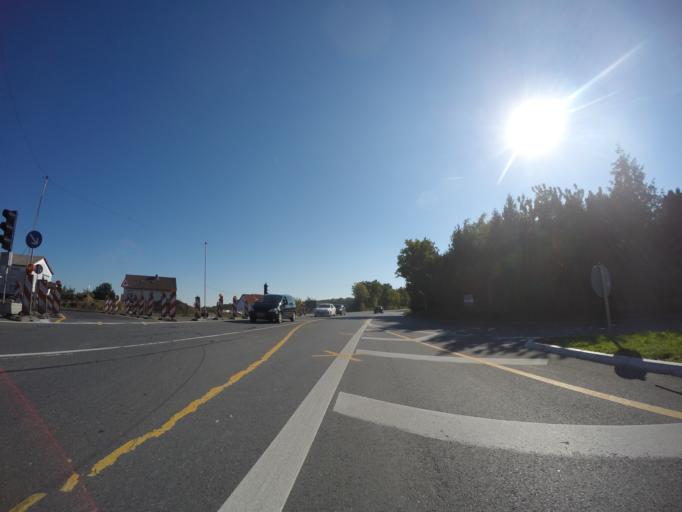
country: DE
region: Bavaria
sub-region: Regierungsbezirk Unterfranken
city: Waldbuttelbrunn
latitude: 49.7915
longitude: 9.8477
